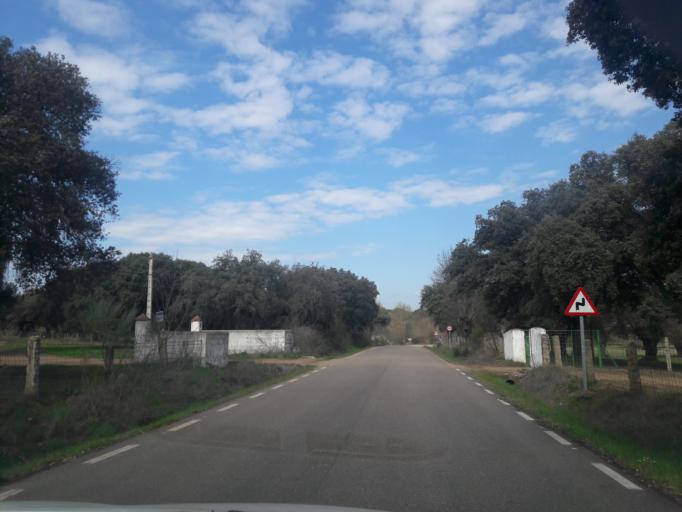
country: ES
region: Castille and Leon
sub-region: Provincia de Salamanca
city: Zamarra
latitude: 40.5561
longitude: -6.4505
